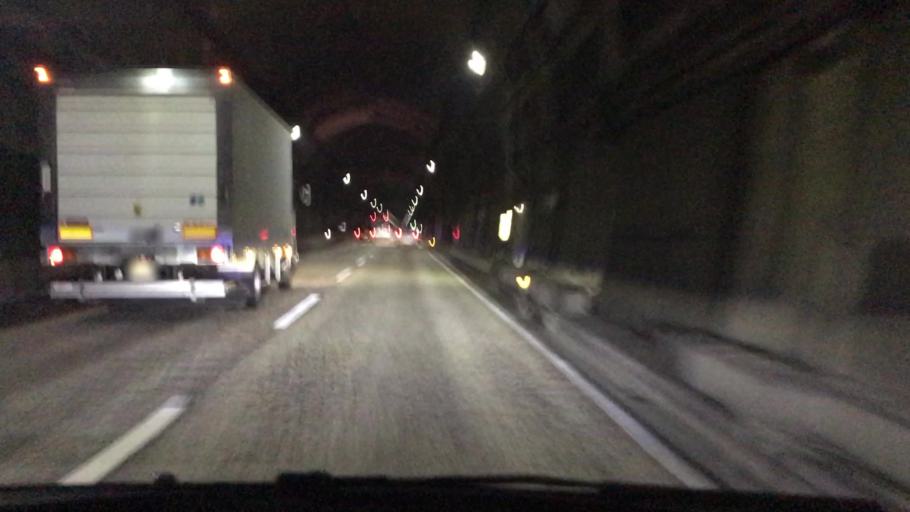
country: JP
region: Hyogo
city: Kobe
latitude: 34.7538
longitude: 135.1645
